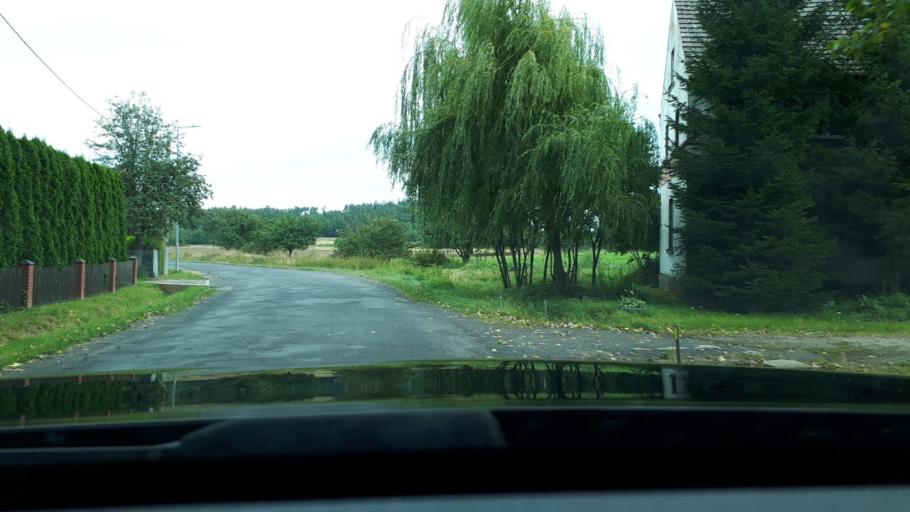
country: PL
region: Lower Silesian Voivodeship
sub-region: Powiat zlotoryjski
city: Olszanica
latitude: 51.1415
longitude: 15.7379
